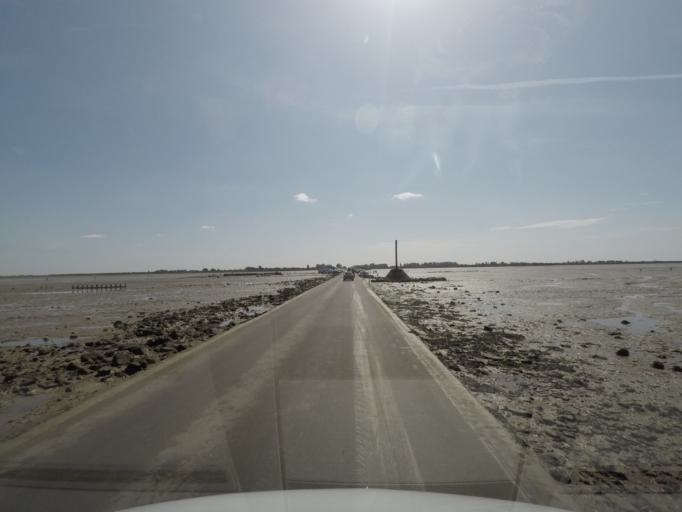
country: FR
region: Pays de la Loire
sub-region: Departement de la Vendee
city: La Barre-de-Monts
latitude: 46.9254
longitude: -2.1109
